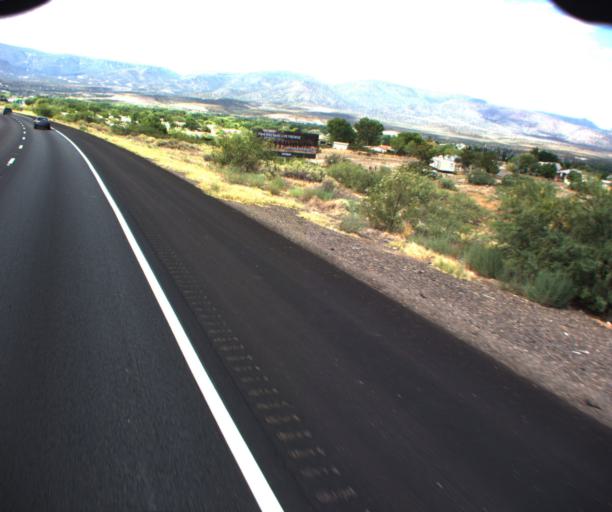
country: US
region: Arizona
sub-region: Yavapai County
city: Camp Verde
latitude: 34.6064
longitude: -111.8696
